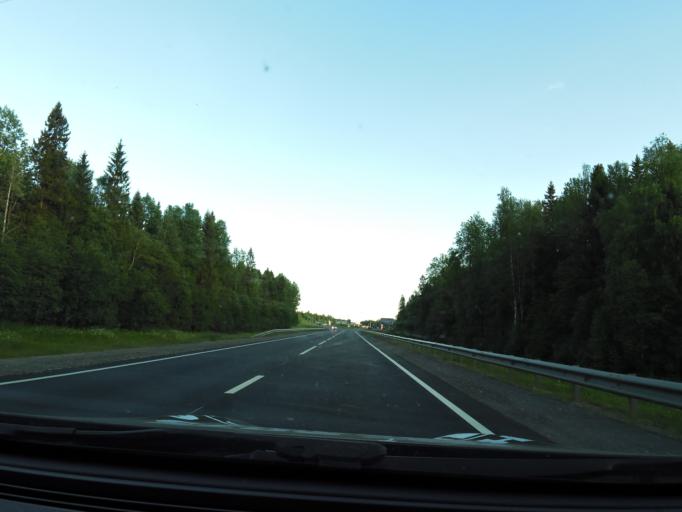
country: RU
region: Vologda
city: Gryazovets
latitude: 58.8892
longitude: 40.1890
